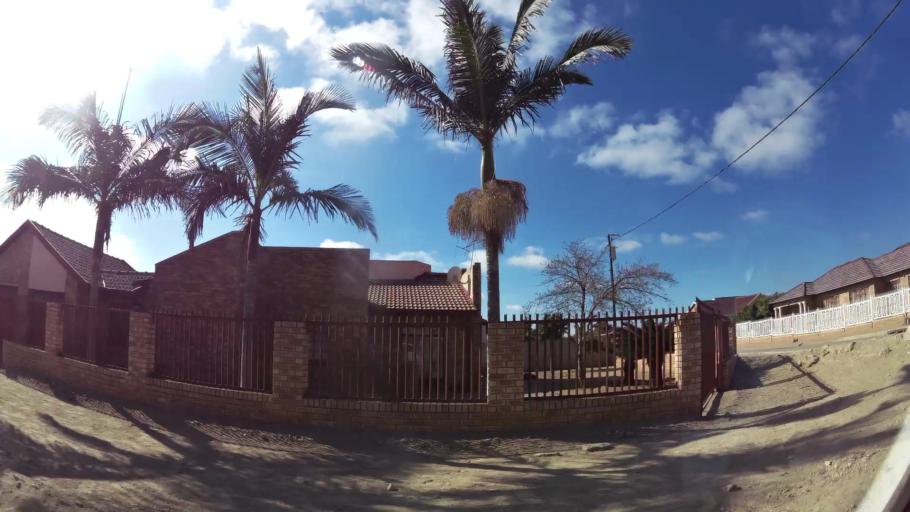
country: ZA
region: Limpopo
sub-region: Capricorn District Municipality
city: Polokwane
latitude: -23.8564
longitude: 29.3695
